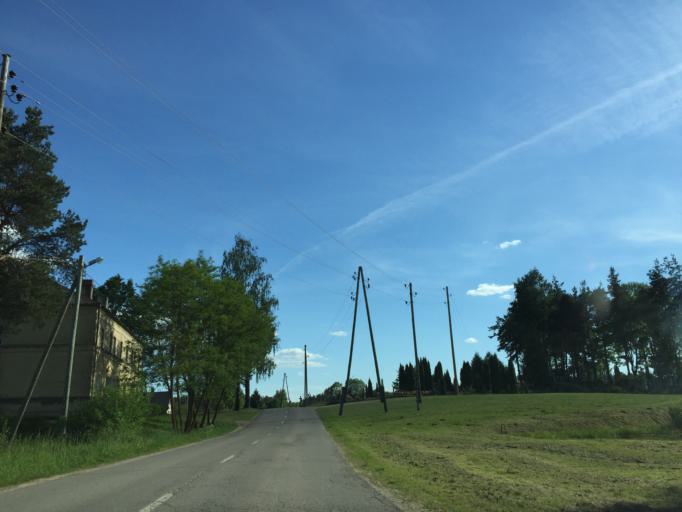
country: LV
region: Rezekne
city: Rezekne
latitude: 56.3446
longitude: 27.1672
